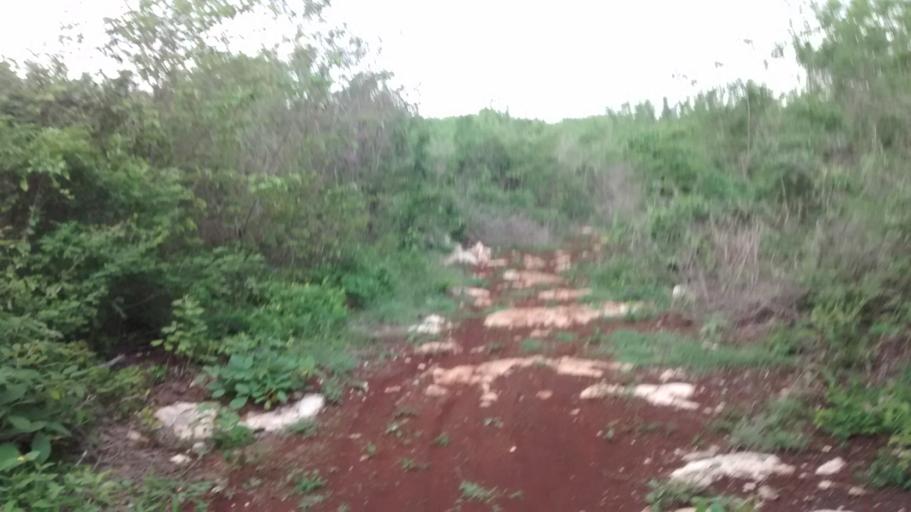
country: MX
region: Yucatan
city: Valladolid
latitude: 20.6877
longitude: -88.1788
